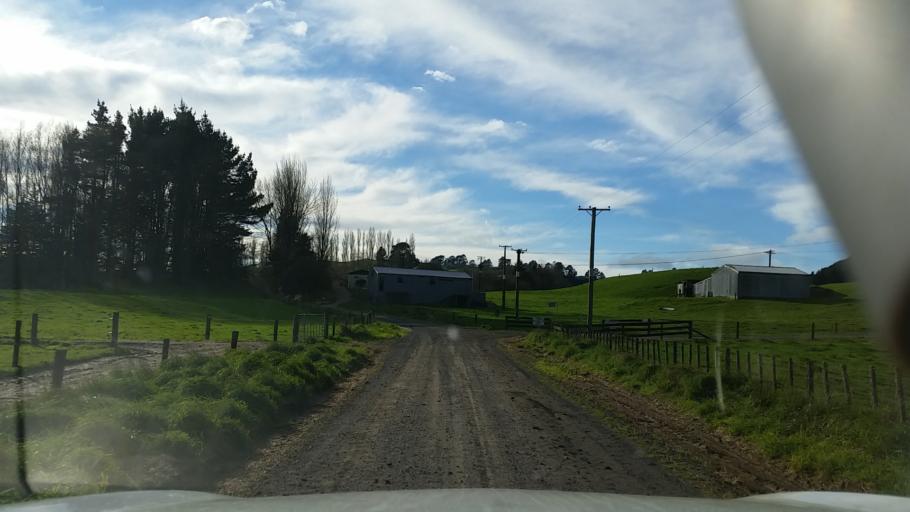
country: NZ
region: Waikato
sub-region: South Waikato District
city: Tokoroa
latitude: -38.3634
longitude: 176.0653
